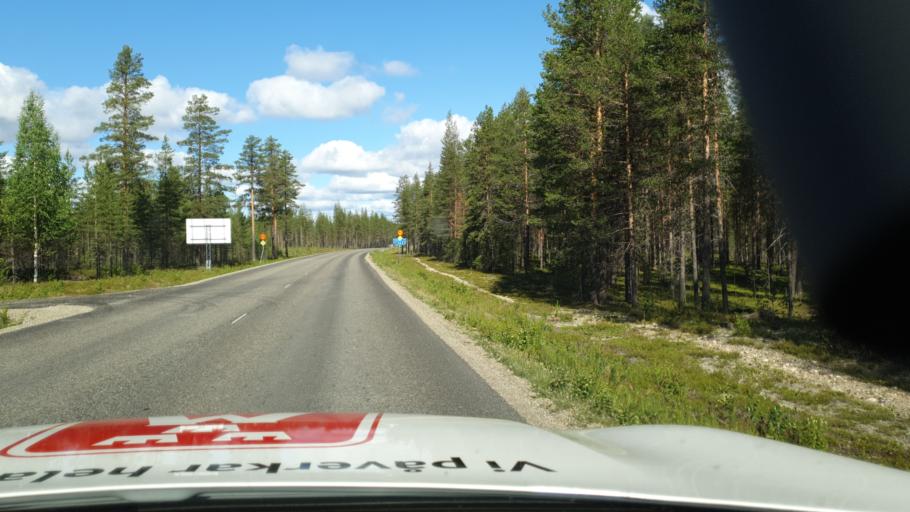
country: SE
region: Vaesterbotten
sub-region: Lycksele Kommun
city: Lycksele
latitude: 64.8266
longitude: 18.7956
